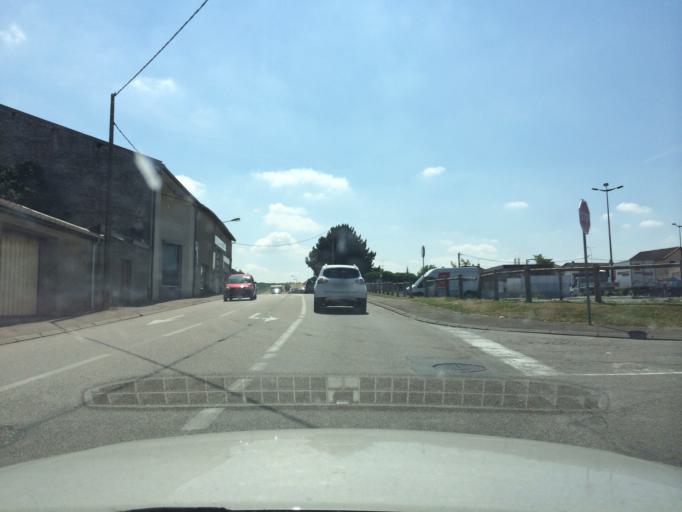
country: FR
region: Lorraine
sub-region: Departement de la Meuse
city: Commercy
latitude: 48.7565
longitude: 5.5855
